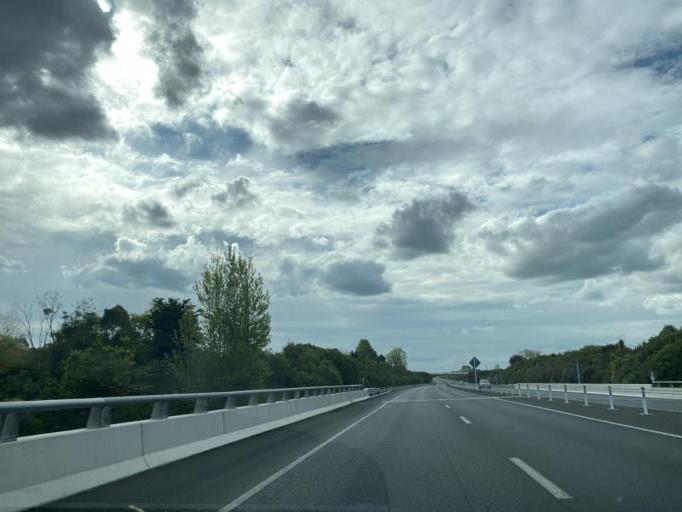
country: NZ
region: Waikato
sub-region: Waipa District
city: Cambridge
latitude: -37.8881
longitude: 175.4956
